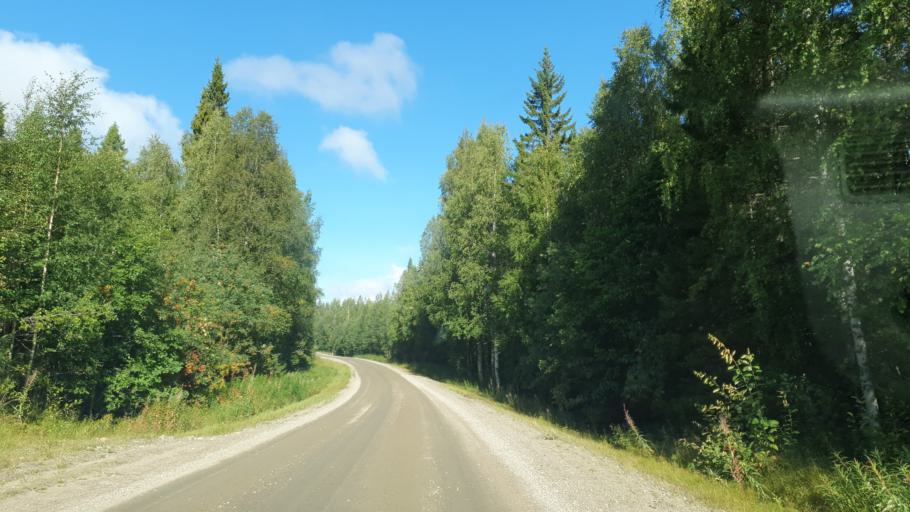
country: FI
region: Kainuu
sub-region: Kehys-Kainuu
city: Kuhmo
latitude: 64.0263
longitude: 29.1804
